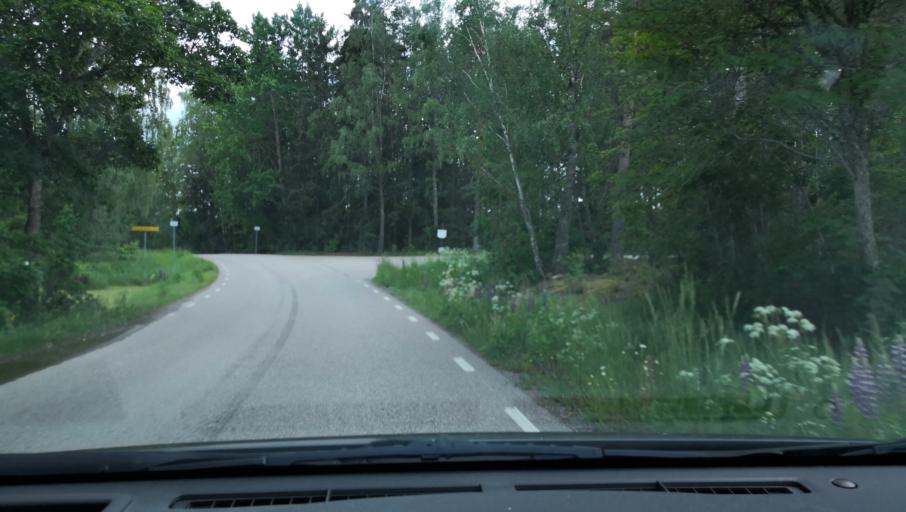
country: SE
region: OErebro
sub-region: Lindesbergs Kommun
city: Fellingsbro
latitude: 59.3318
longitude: 15.6674
